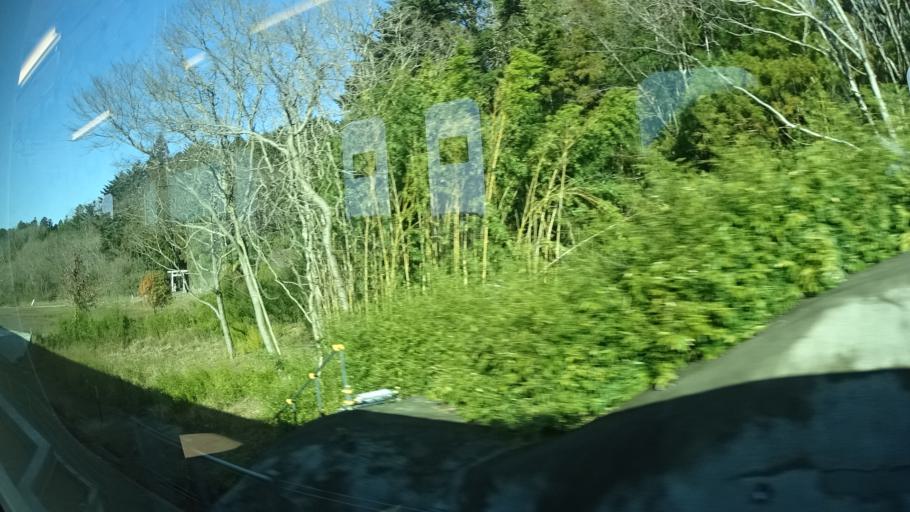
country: JP
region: Fukushima
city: Namie
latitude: 37.4191
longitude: 140.9985
